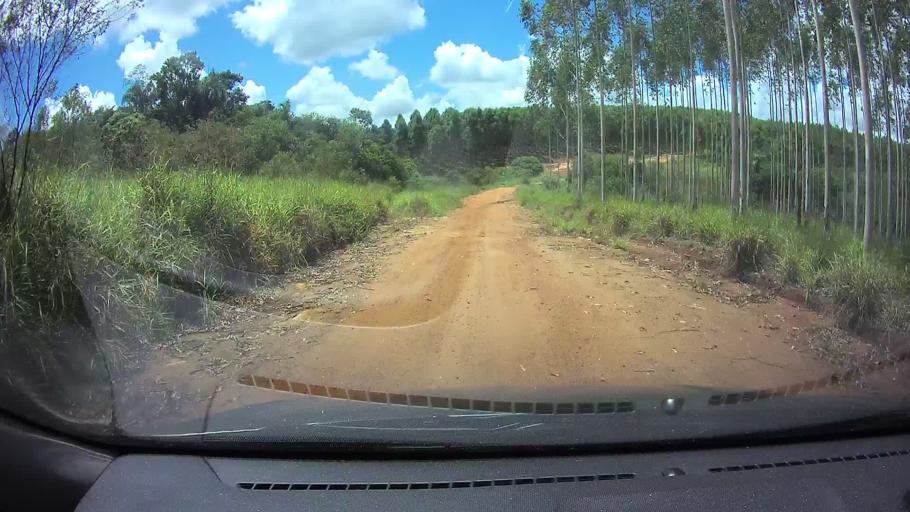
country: PY
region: Paraguari
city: La Colmena
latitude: -25.9650
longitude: -56.7417
